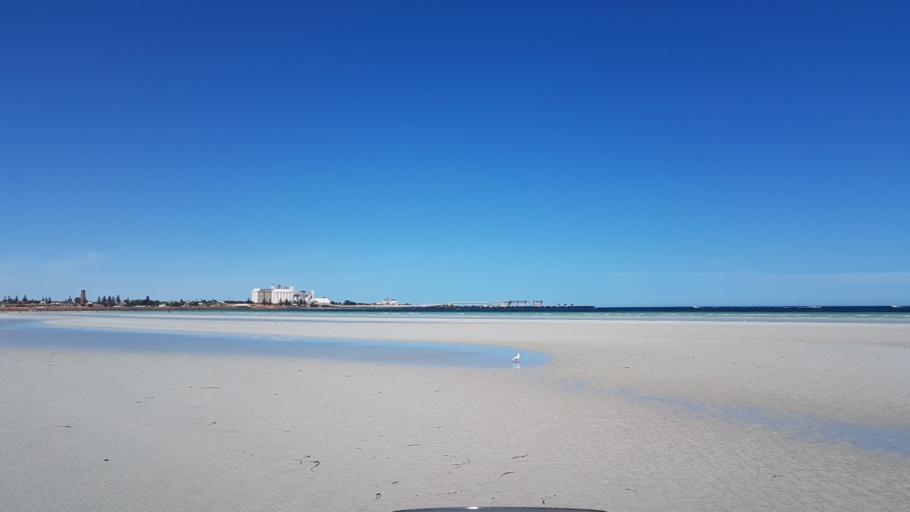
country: AU
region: South Australia
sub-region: Copper Coast
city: Wallaroo
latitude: -33.9119
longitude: 137.6298
